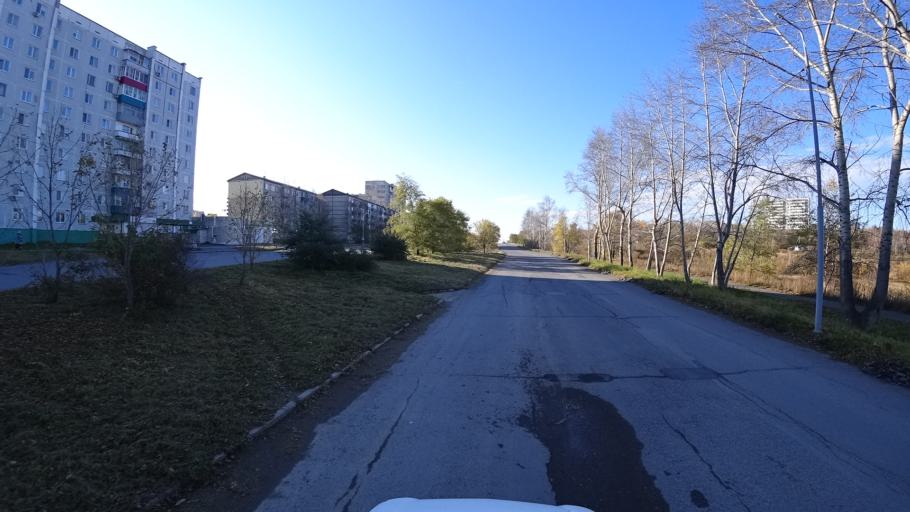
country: RU
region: Khabarovsk Krai
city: Amursk
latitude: 50.2460
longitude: 136.9158
